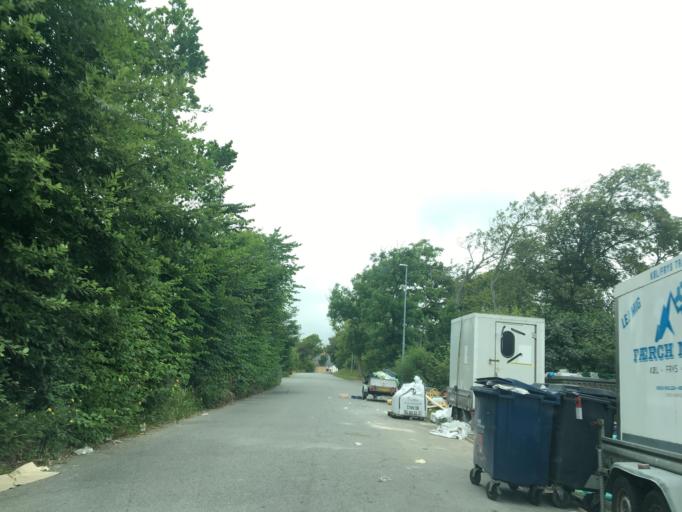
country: DK
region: North Denmark
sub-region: Thisted Kommune
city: Hurup
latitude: 56.7509
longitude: 8.4184
